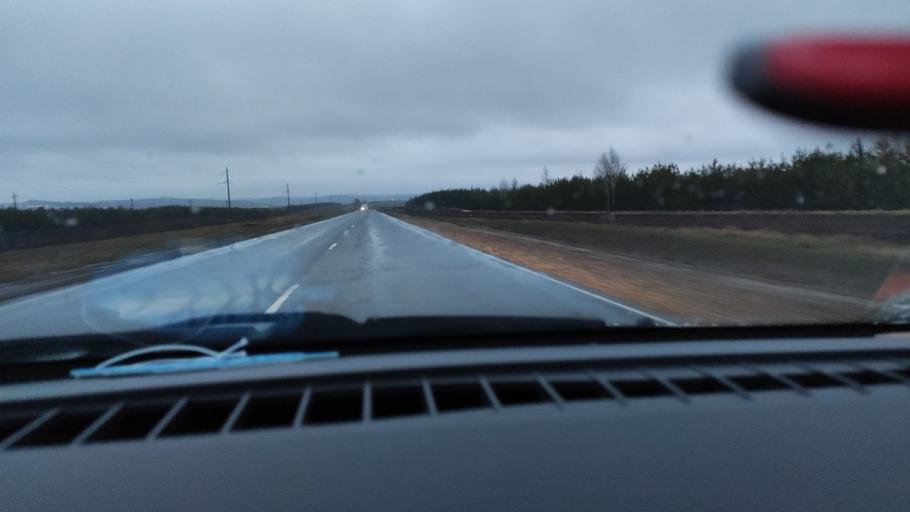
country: RU
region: Udmurtiya
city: Alnashi
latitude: 56.2111
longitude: 52.4358
